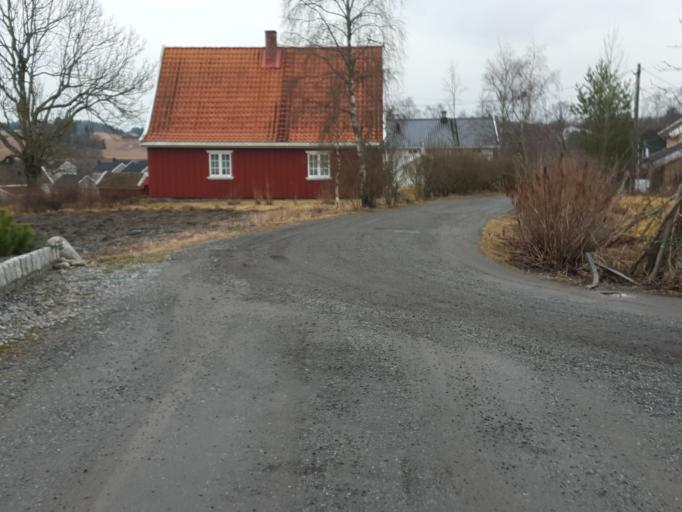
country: NO
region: Akershus
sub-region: Ski
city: Ski
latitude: 59.6846
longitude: 10.8924
